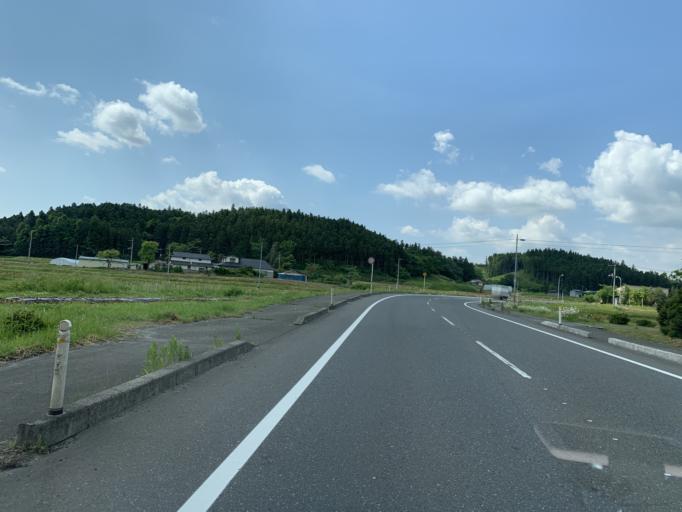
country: JP
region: Miyagi
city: Furukawa
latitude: 38.7312
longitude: 140.9578
